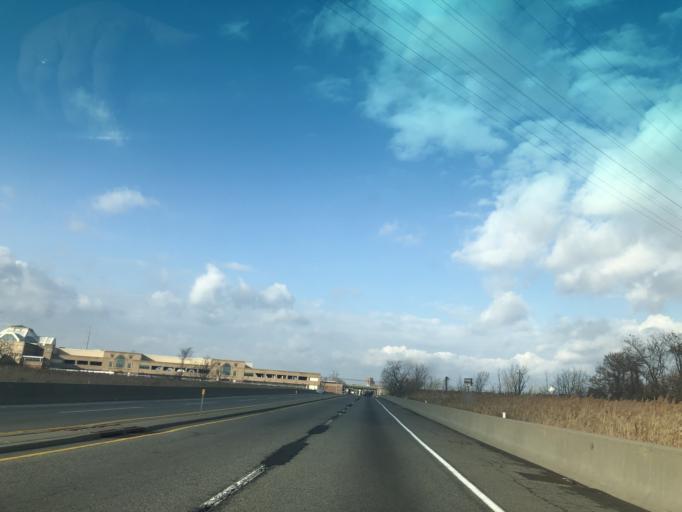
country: US
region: New Jersey
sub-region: Hudson County
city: Jersey City
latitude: 40.7580
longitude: -74.0713
